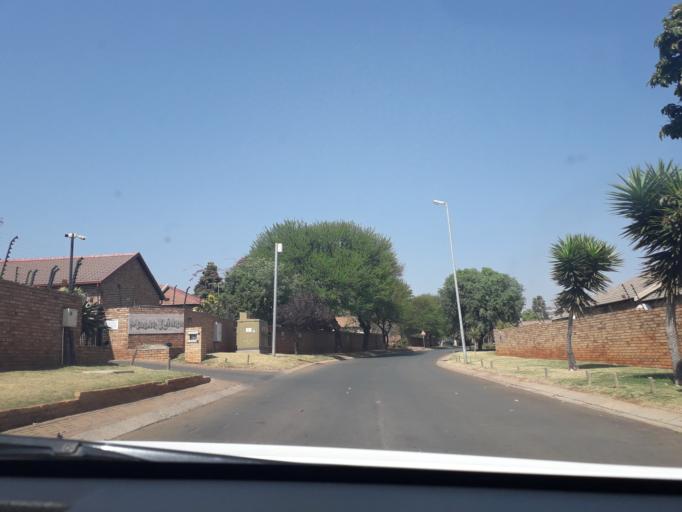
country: ZA
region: Gauteng
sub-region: City of Johannesburg Metropolitan Municipality
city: Roodepoort
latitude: -26.1261
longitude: 27.9369
